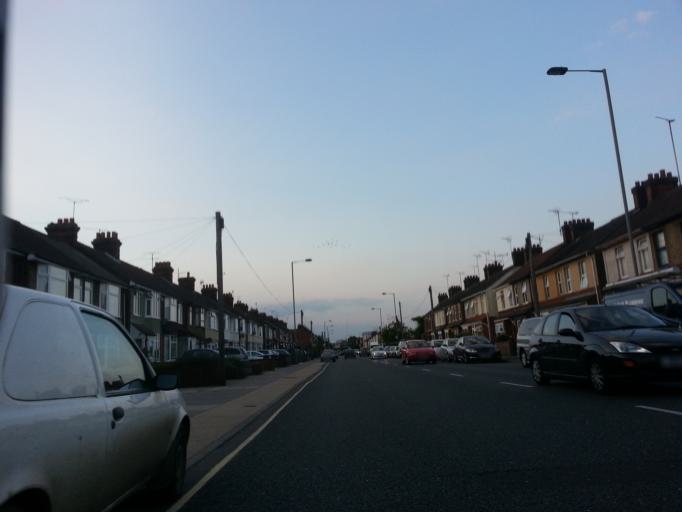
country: GB
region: England
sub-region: Suffolk
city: Ipswich
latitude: 52.0386
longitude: 1.1511
